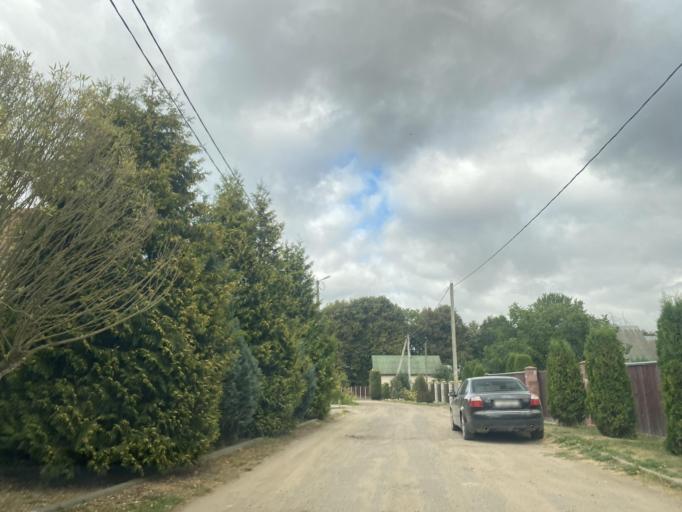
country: BY
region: Minsk
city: Bal'shavik
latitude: 53.9878
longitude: 27.5868
